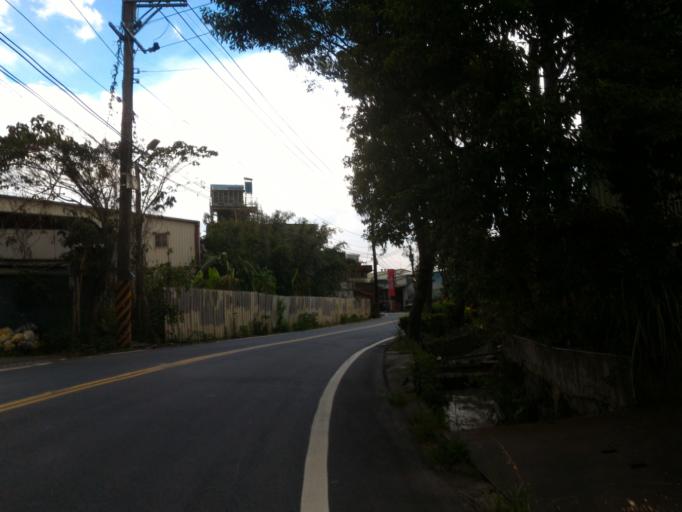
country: TW
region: Taiwan
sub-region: Taoyuan
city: Taoyuan
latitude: 24.9568
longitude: 121.3976
